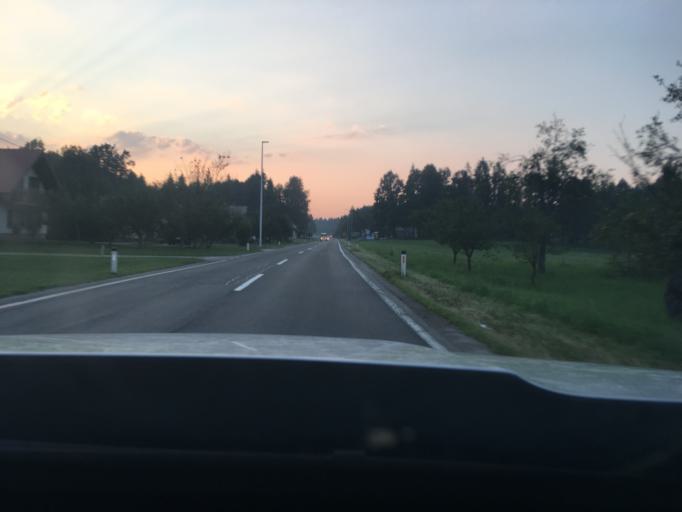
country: SI
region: Kocevje
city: Kocevje
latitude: 45.6747
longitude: 14.8286
